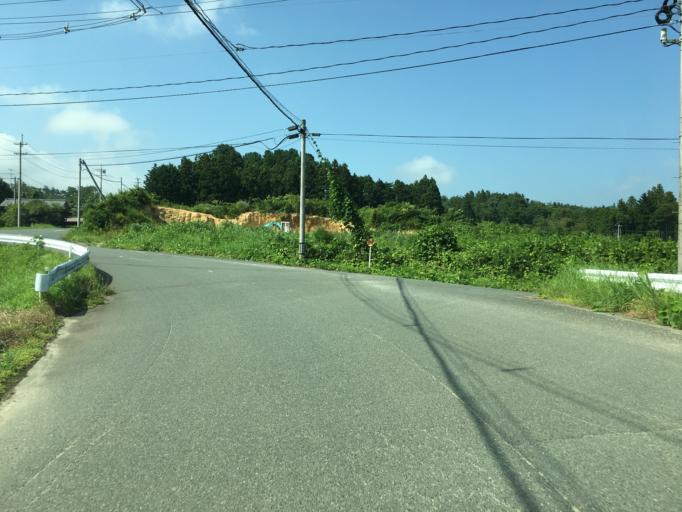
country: JP
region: Miyagi
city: Marumori
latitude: 37.8933
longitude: 140.8910
